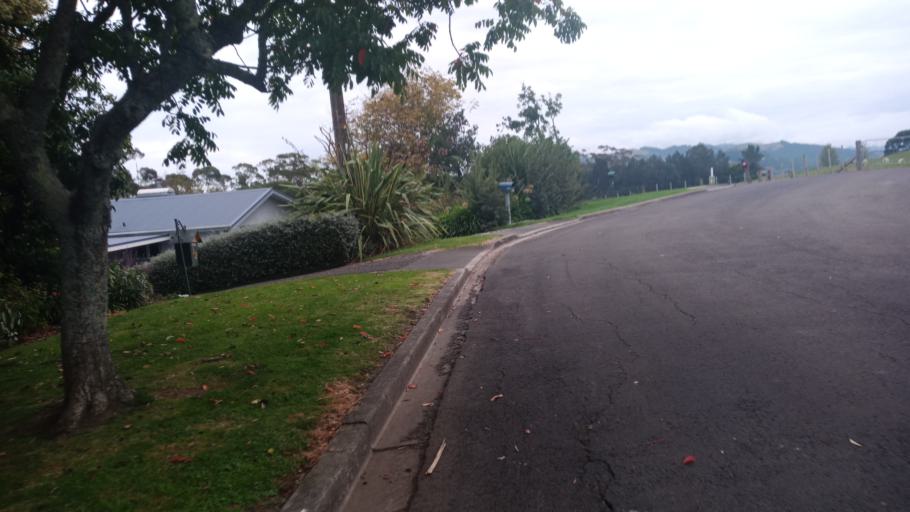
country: NZ
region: Gisborne
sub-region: Gisborne District
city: Gisborne
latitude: -38.6825
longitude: 178.0425
